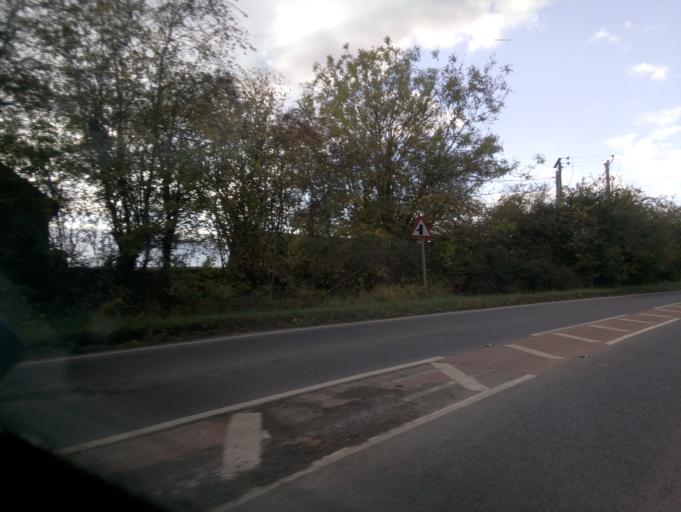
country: GB
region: England
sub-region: Herefordshire
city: Withington
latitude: 52.0639
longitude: -2.6304
